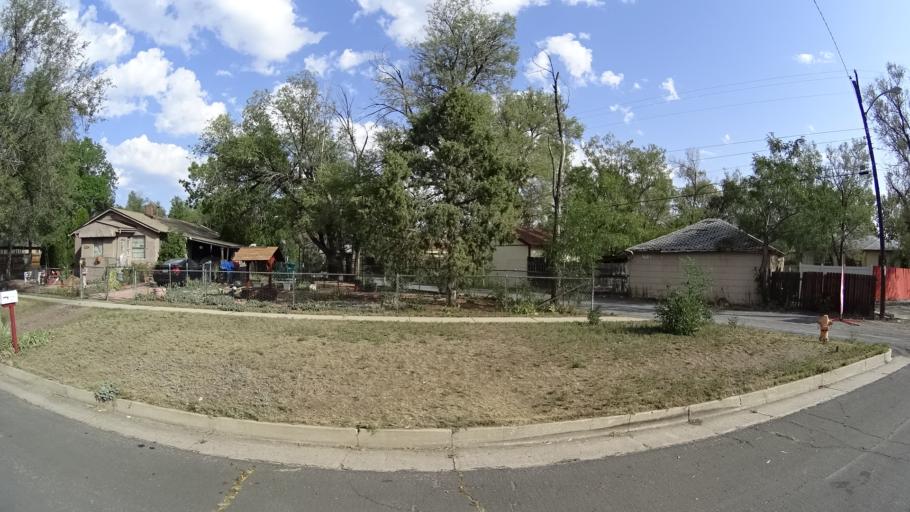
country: US
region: Colorado
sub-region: El Paso County
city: Colorado Springs
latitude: 38.8239
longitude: -104.8016
